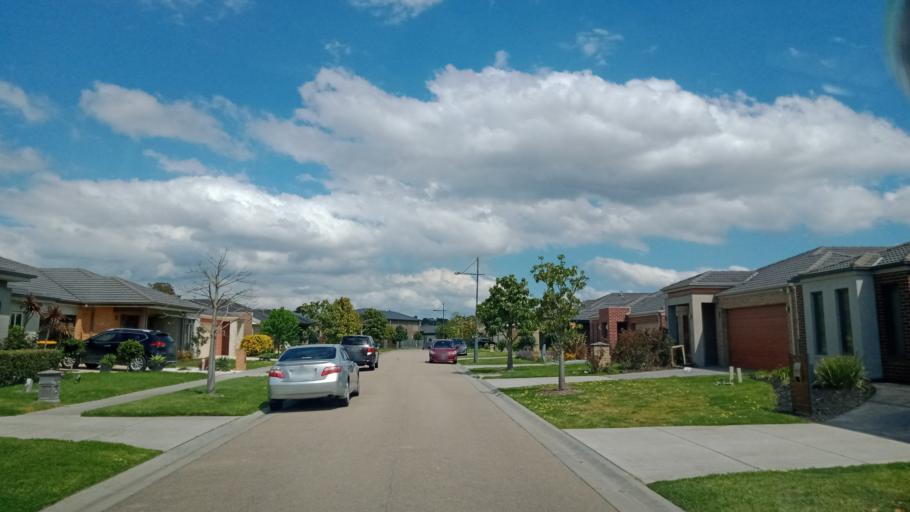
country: AU
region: Victoria
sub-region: Frankston
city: Sandhurst
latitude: -38.0822
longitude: 145.1987
